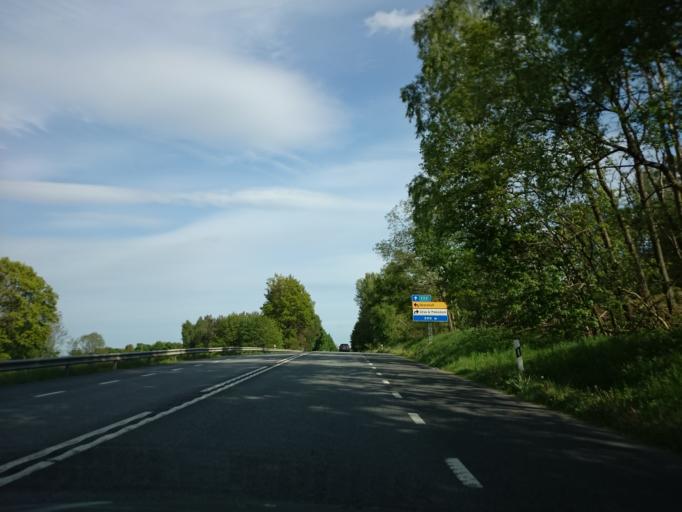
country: SE
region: Skane
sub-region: Kristianstads Kommun
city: Onnestad
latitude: 55.9347
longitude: 13.9180
